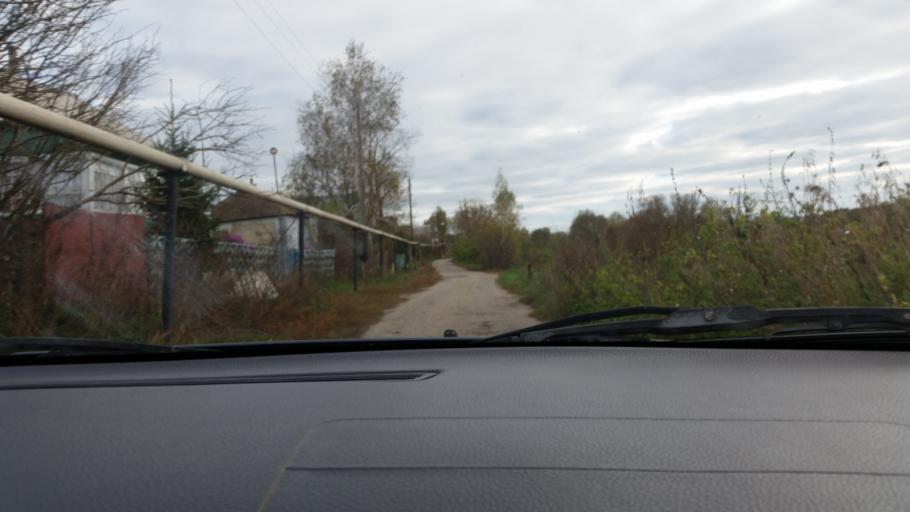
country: RU
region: Lipetsk
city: Gryazi
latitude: 52.4529
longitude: 39.9821
